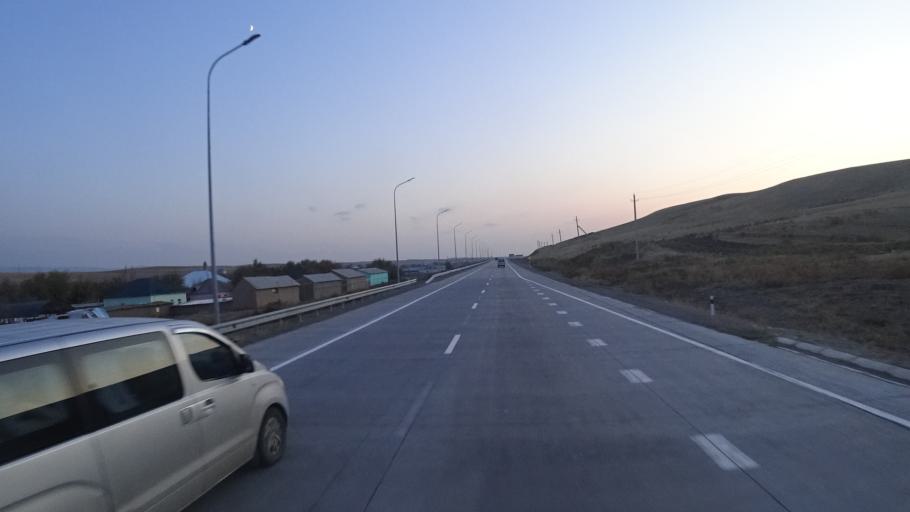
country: KZ
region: Ongtustik Qazaqstan
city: Qazyqurt
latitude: 41.9020
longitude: 69.4557
